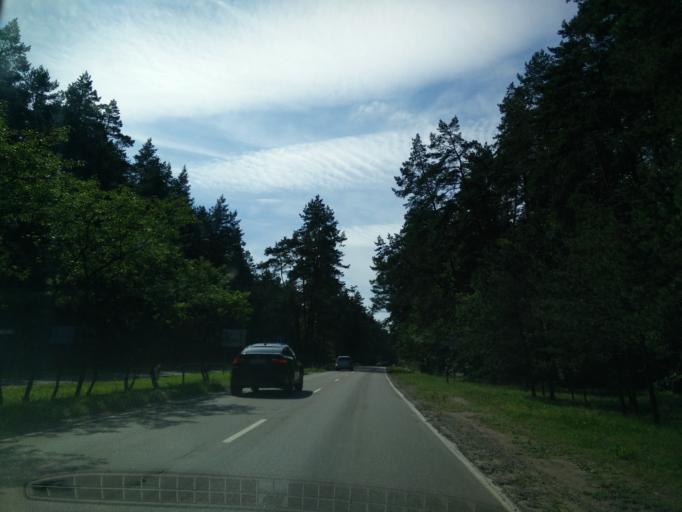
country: LT
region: Vilnius County
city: Rasos
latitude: 54.7475
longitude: 25.3570
